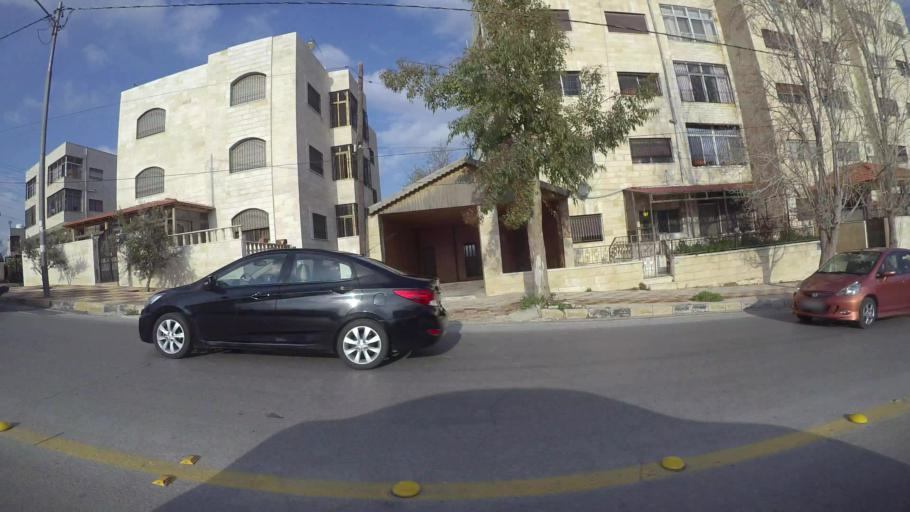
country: JO
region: Amman
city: Al Jubayhah
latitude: 31.9838
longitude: 35.8606
